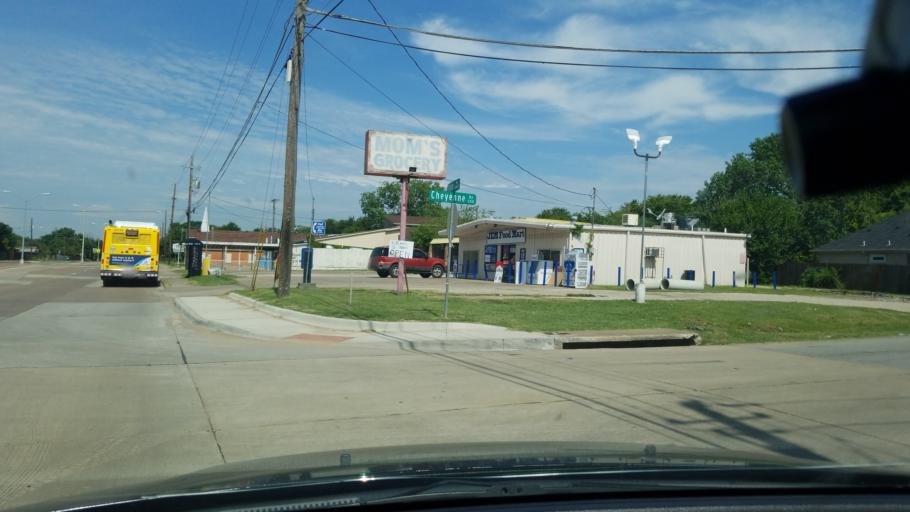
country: US
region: Texas
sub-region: Dallas County
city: Balch Springs
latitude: 32.7195
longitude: -96.6392
